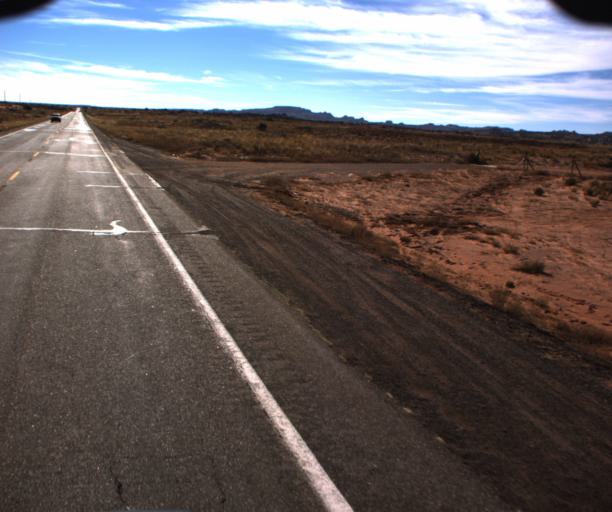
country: US
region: Arizona
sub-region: Coconino County
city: Kaibito
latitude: 36.6098
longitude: -111.1836
